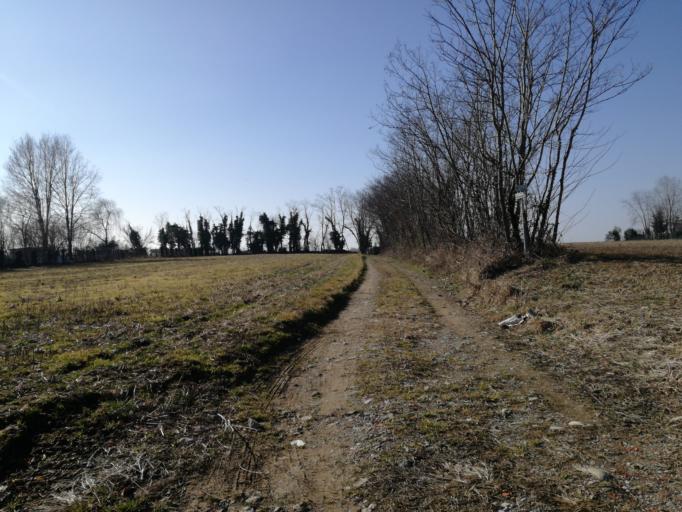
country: IT
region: Lombardy
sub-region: Provincia di Lecco
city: Verderio Inferiore
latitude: 45.6541
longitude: 9.4325
